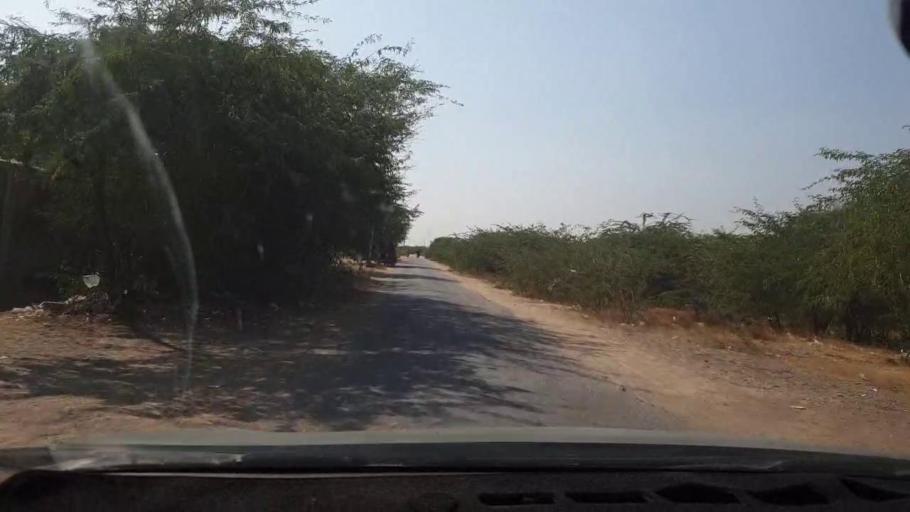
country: PK
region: Sindh
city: Malir Cantonment
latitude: 25.1292
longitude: 67.2279
